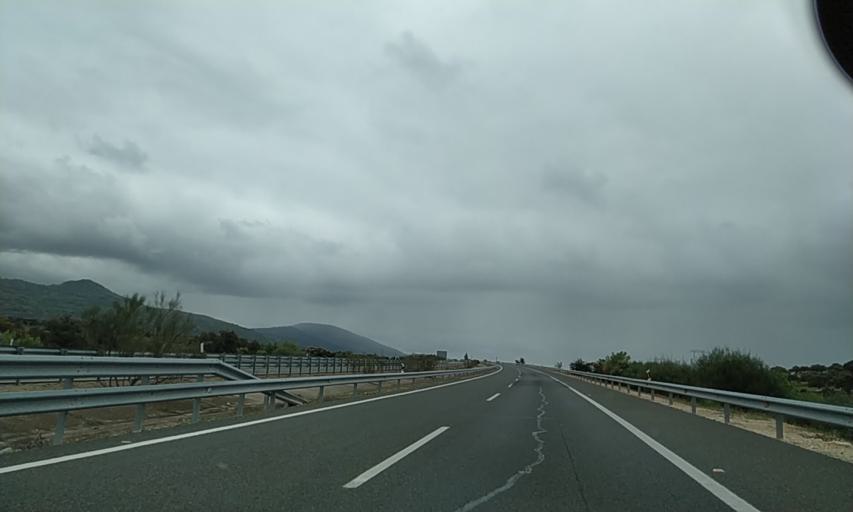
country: ES
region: Extremadura
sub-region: Provincia de Caceres
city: Jarilla
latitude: 40.1814
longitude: -6.0159
